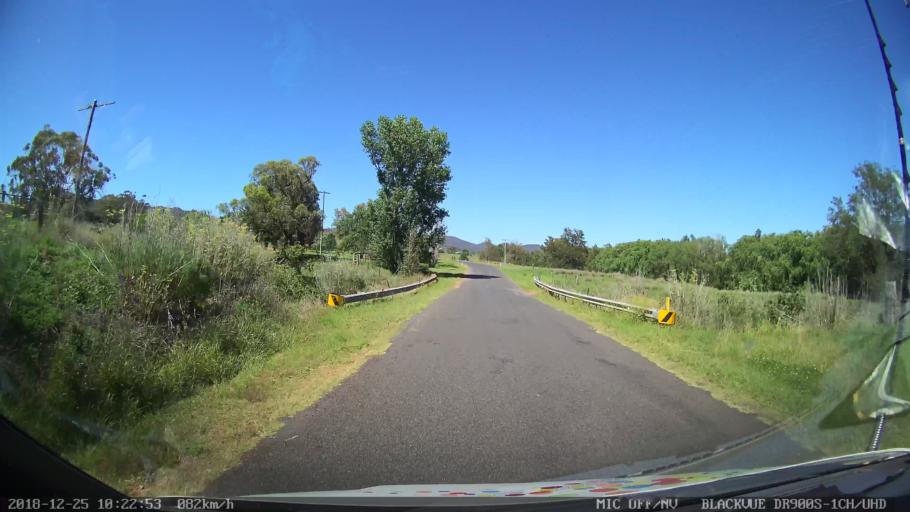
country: AU
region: New South Wales
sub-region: Muswellbrook
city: Denman
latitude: -32.3801
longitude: 150.5274
